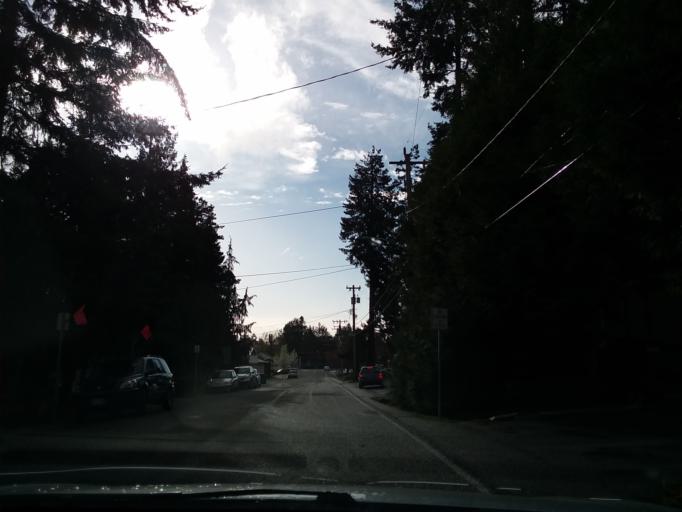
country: US
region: Washington
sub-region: King County
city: Lake Forest Park
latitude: 47.7575
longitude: -122.3106
